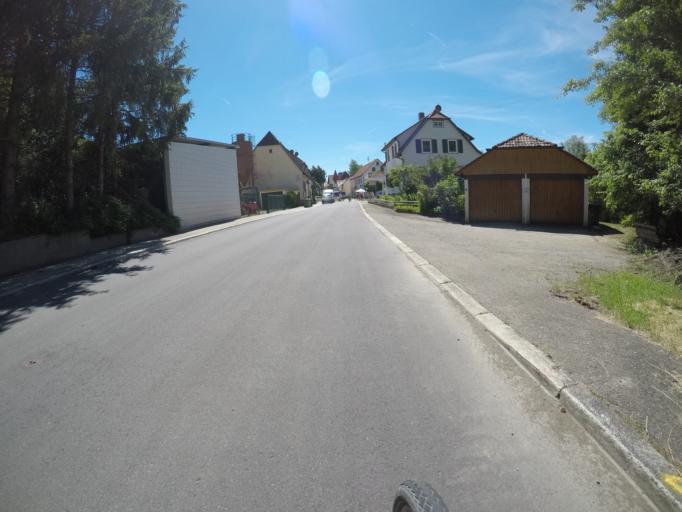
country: DE
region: Baden-Wuerttemberg
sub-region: Karlsruhe Region
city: Friolzheim
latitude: 48.8069
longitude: 8.8213
